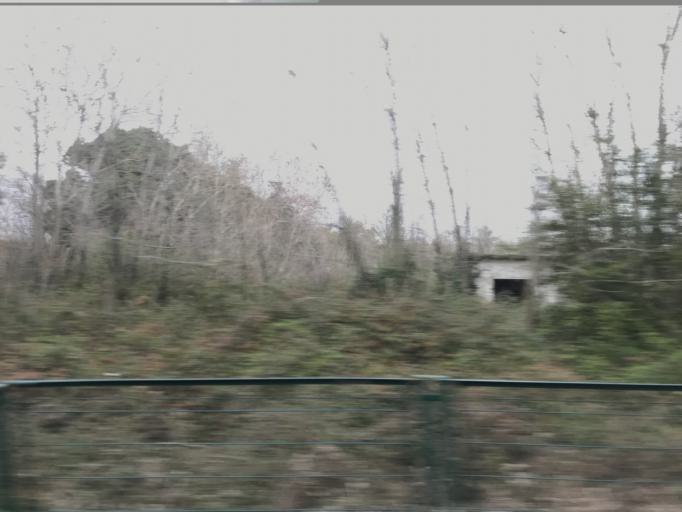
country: TR
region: Istanbul
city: Icmeler
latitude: 40.8117
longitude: 29.3422
